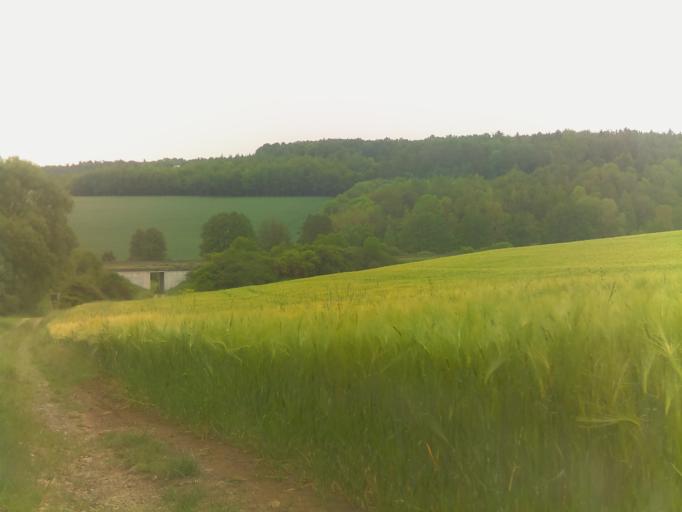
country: DE
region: Thuringia
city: Henneberg
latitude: 50.4514
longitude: 10.3686
